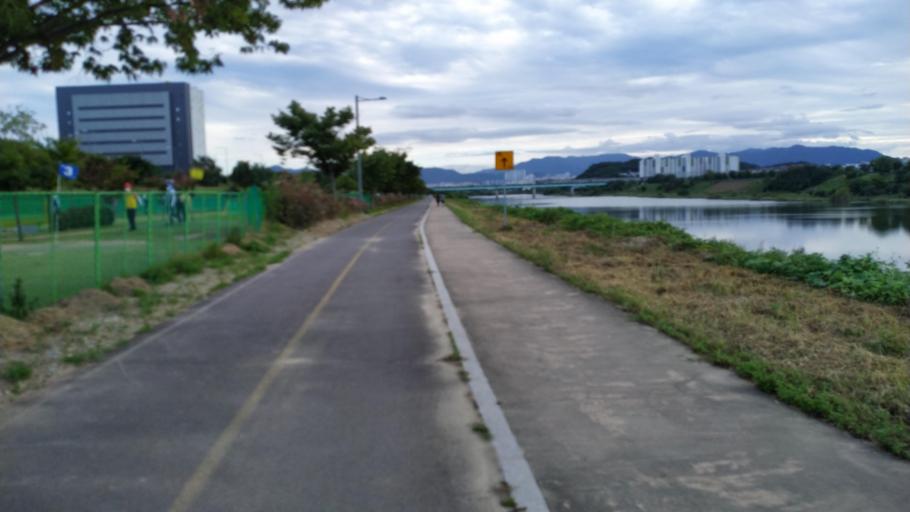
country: KR
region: Daegu
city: Daegu
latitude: 35.9257
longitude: 128.6324
